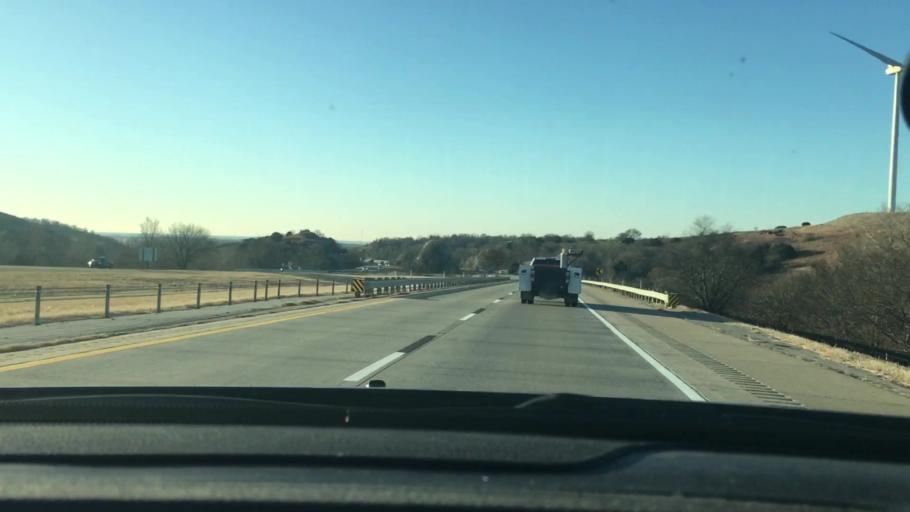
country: US
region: Oklahoma
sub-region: Murray County
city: Davis
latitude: 34.3619
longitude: -97.1482
